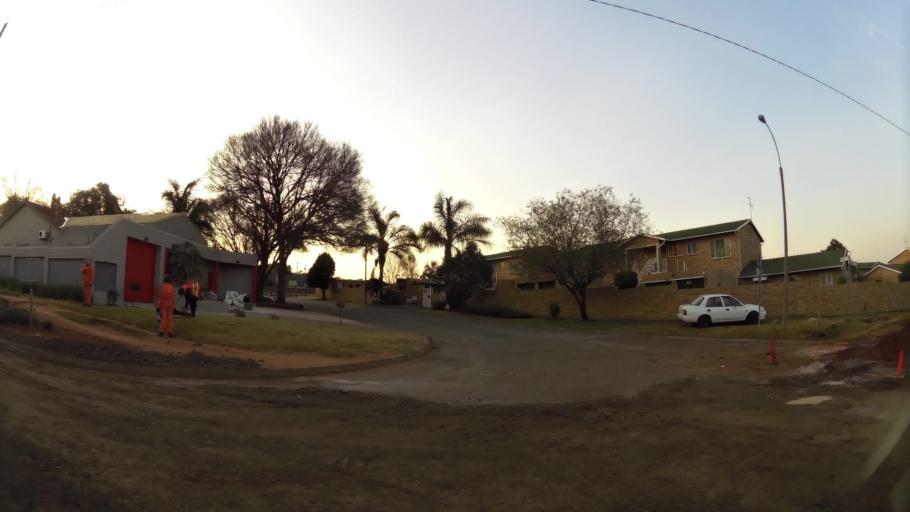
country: ZA
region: Gauteng
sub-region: City of Johannesburg Metropolitan Municipality
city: Modderfontein
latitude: -26.0695
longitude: 28.2261
